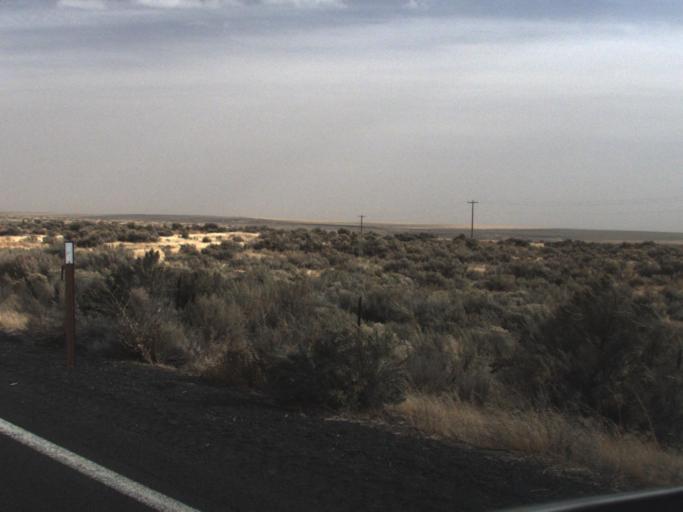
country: US
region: Washington
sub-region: Adams County
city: Ritzville
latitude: 47.4260
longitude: -118.7089
